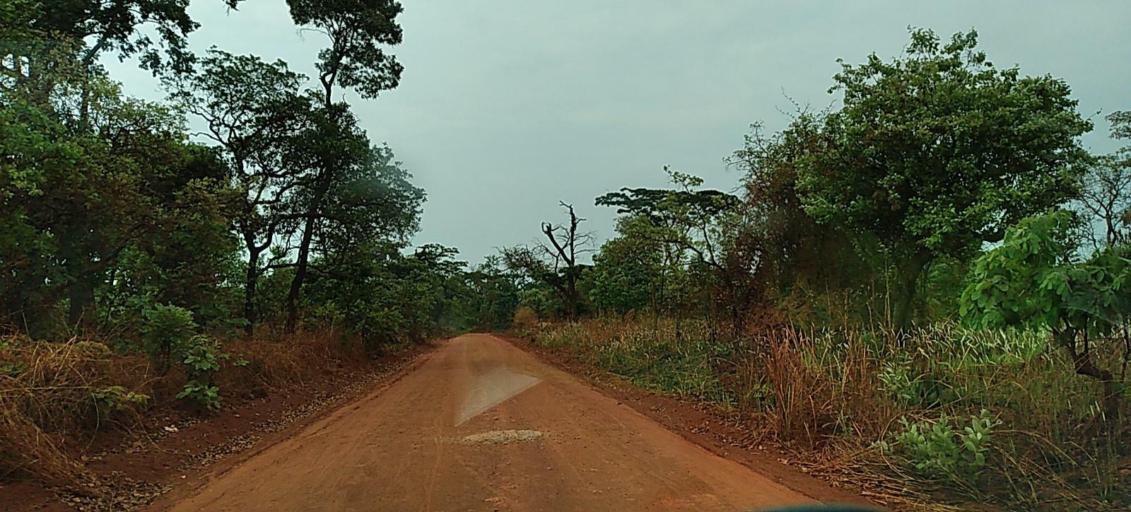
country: ZM
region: North-Western
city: Solwezi
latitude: -12.2208
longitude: 26.5099
